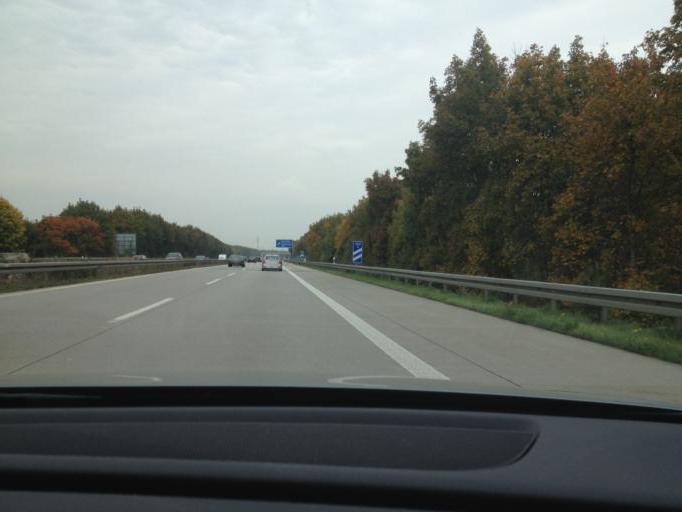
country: DE
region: Baden-Wuerttemberg
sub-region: Karlsruhe Region
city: Hockenheim
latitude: 49.3504
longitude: 8.5519
